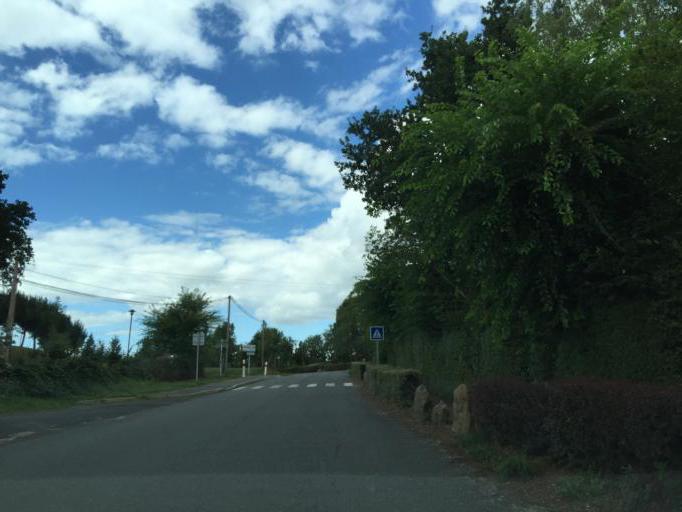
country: FR
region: Midi-Pyrenees
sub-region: Departement de l'Aveyron
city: Pont-de-Salars
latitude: 44.2897
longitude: 2.7271
